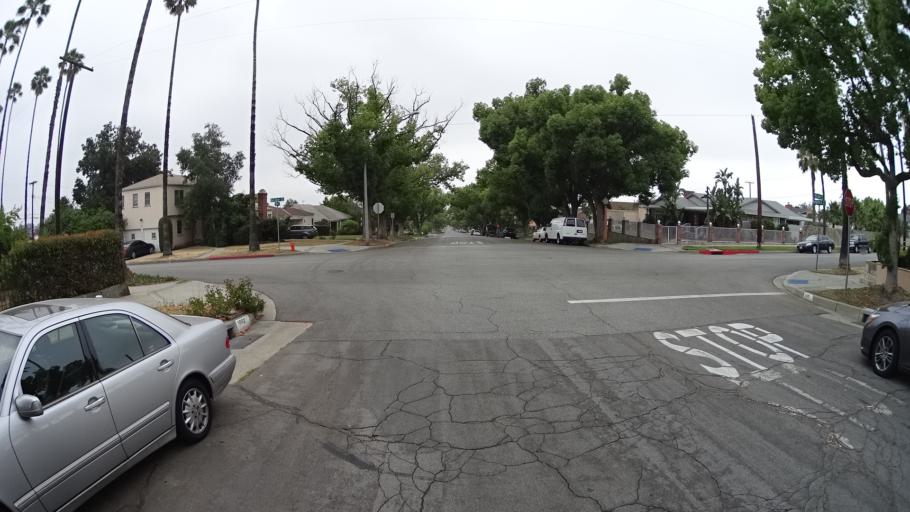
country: US
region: California
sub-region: Los Angeles County
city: Burbank
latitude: 34.1895
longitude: -118.2978
